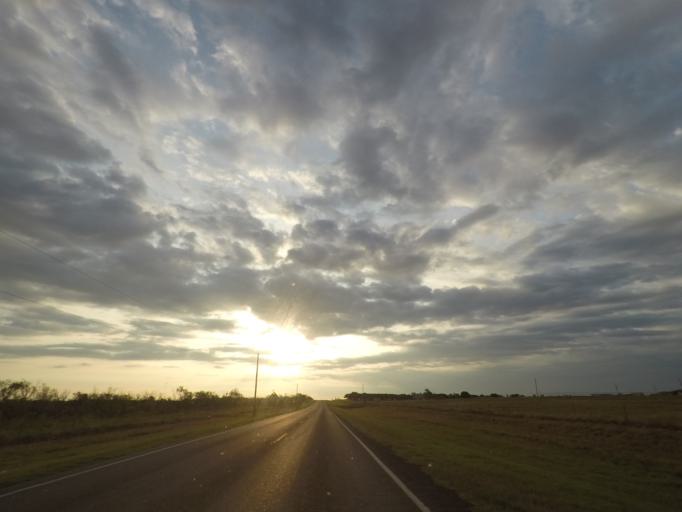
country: US
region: Oklahoma
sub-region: Jefferson County
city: Waurika
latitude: 34.1591
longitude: -98.0364
